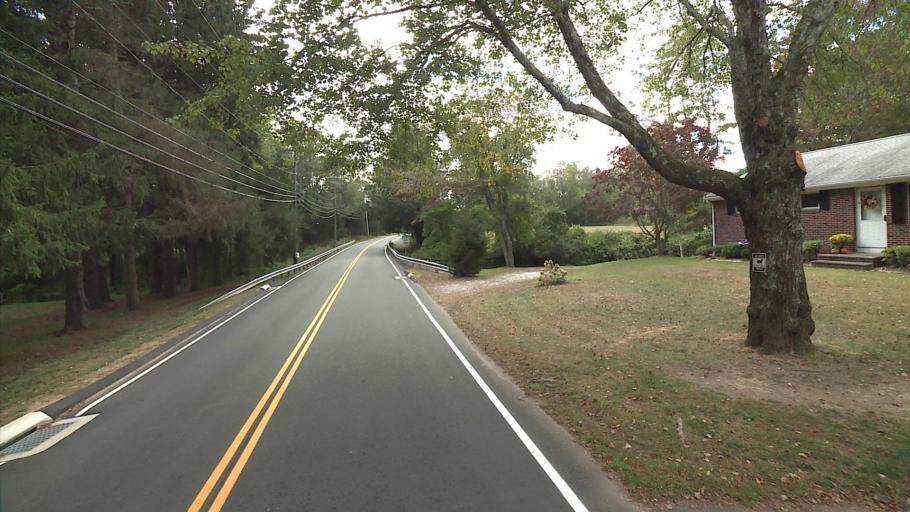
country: US
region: Connecticut
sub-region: Middlesex County
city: Chester Center
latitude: 41.4151
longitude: -72.4374
